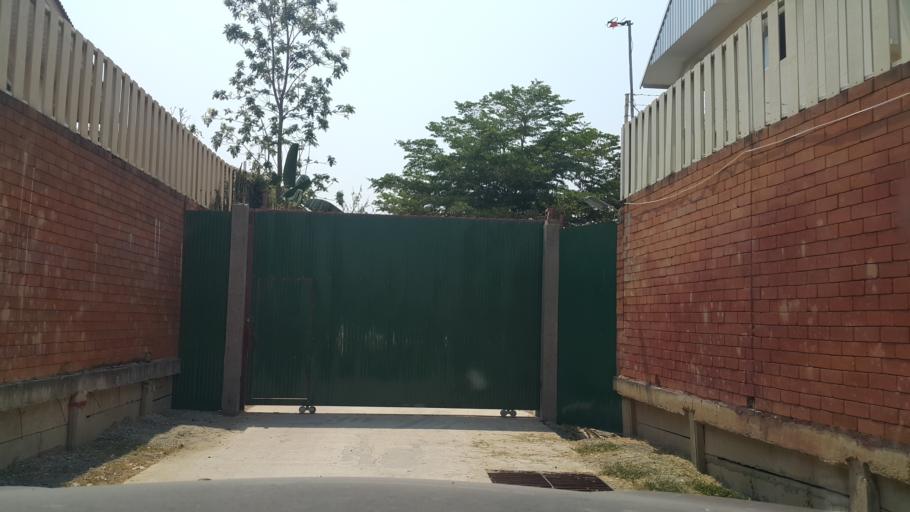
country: TH
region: Chiang Mai
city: Saraphi
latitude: 18.7587
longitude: 99.0351
